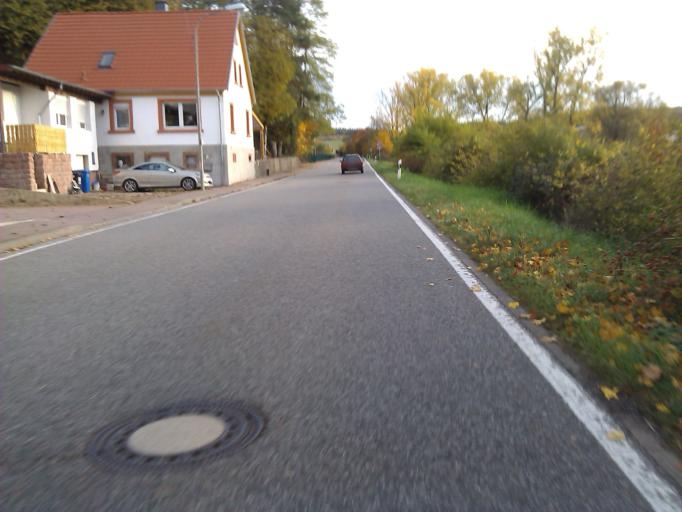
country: DE
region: Rheinland-Pfalz
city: Schneckenhausen
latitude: 49.5375
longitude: 7.7424
